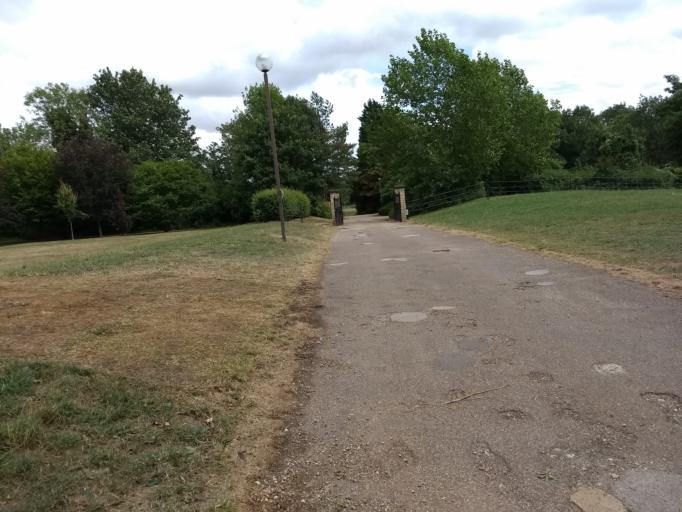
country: GB
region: England
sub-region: Milton Keynes
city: Milton Keynes
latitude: 52.0731
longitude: -0.7561
